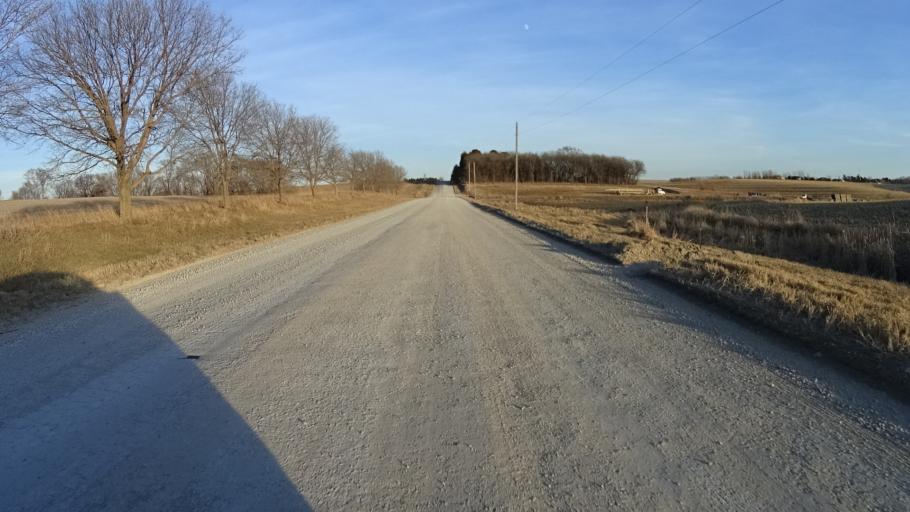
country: US
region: Nebraska
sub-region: Sarpy County
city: Springfield
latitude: 41.1326
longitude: -96.1180
